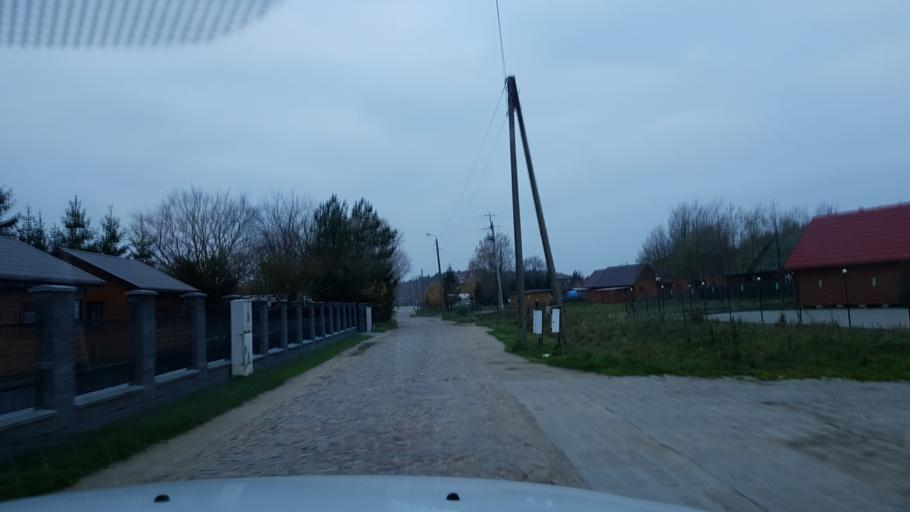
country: PL
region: West Pomeranian Voivodeship
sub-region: Powiat slawienski
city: Darlowo
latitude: 54.5069
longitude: 16.4742
